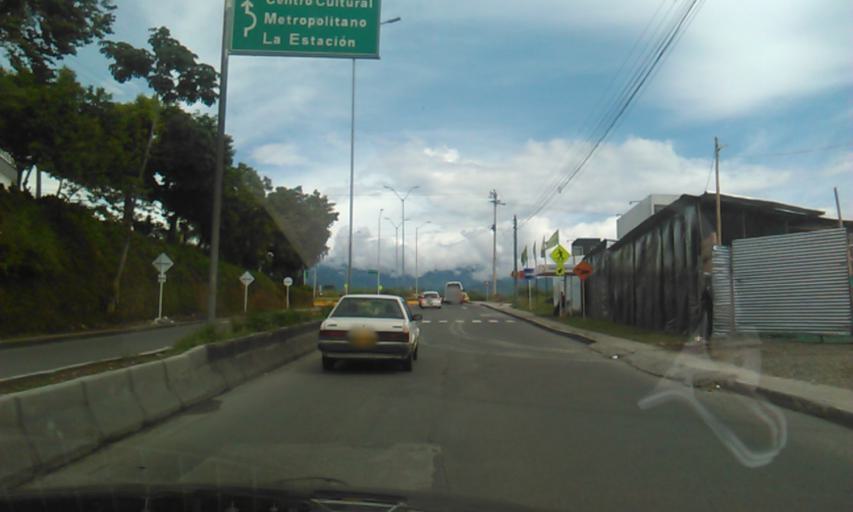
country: CO
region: Quindio
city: Armenia
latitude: 4.5310
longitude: -75.7035
